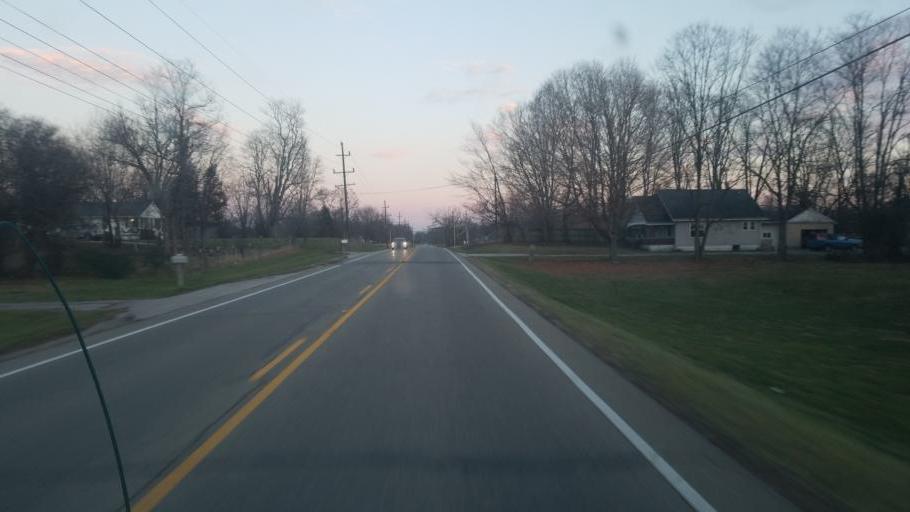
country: US
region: Indiana
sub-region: Lawrence County
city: Bedford
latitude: 38.8750
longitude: -86.3663
